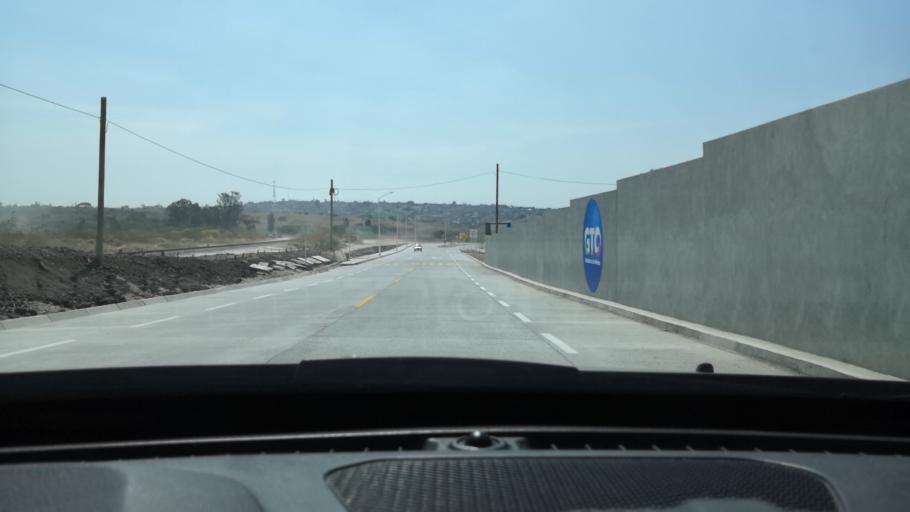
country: MX
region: Guanajuato
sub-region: Purisima del Rincon
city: Potrerillos (Guanajal)
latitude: 21.0606
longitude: -101.8694
